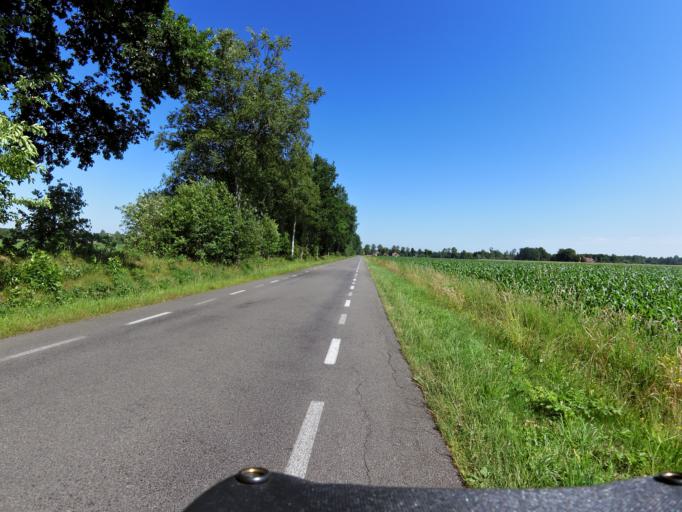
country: NL
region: Overijssel
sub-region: Gemeente Twenterand
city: Den Ham
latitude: 52.5324
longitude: 6.4455
